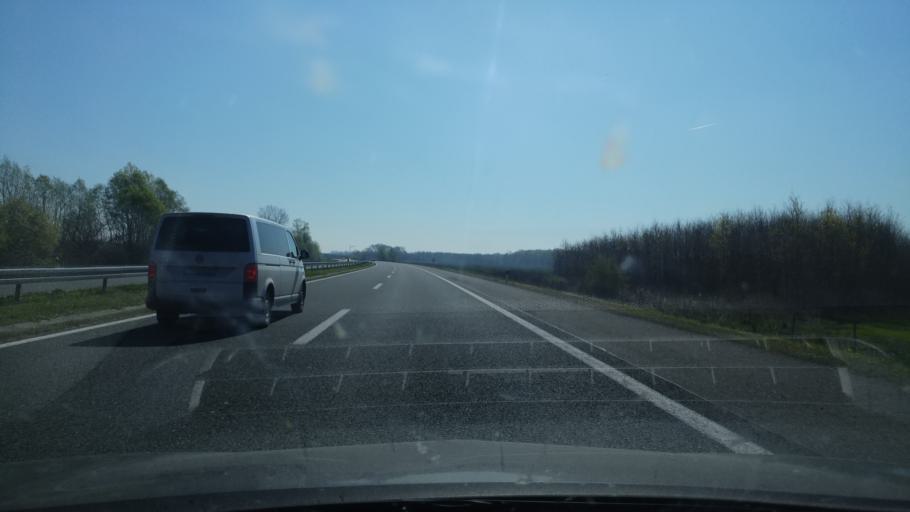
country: HR
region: Brodsko-Posavska
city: Garcin
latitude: 45.1602
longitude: 18.1789
